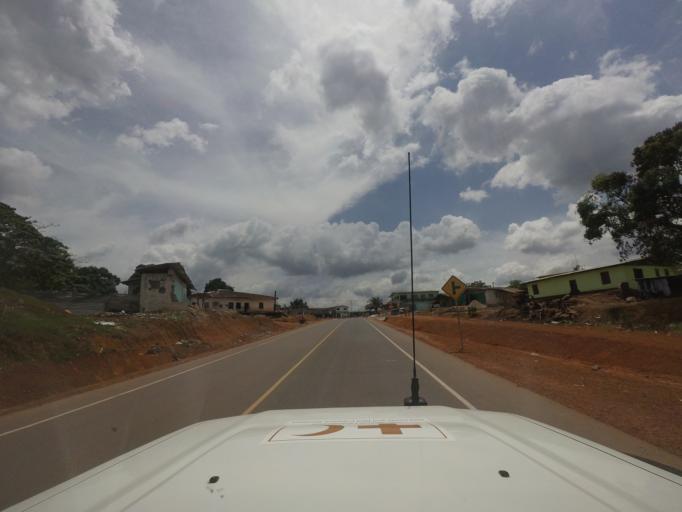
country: LR
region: Nimba
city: Sanniquellie
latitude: 7.2350
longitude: -8.9841
